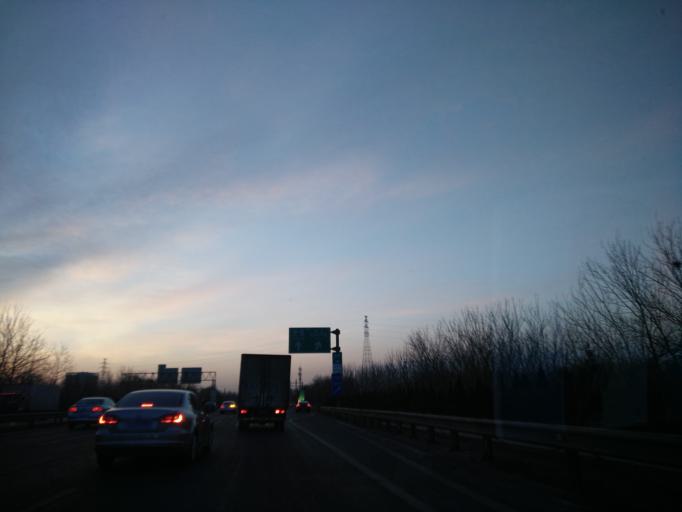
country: CN
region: Beijing
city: Jiugong
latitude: 39.8150
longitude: 116.5044
